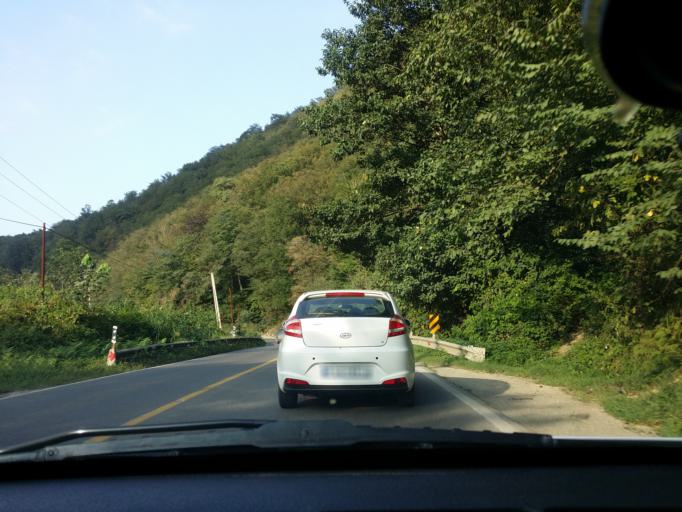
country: IR
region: Mazandaran
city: Chalus
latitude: 36.5701
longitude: 51.3799
